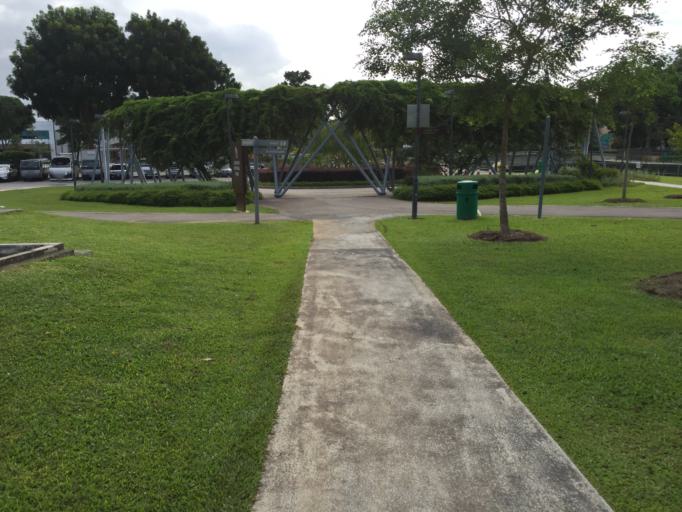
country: MY
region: Johor
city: Johor Bahru
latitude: 1.3387
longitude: 103.7089
